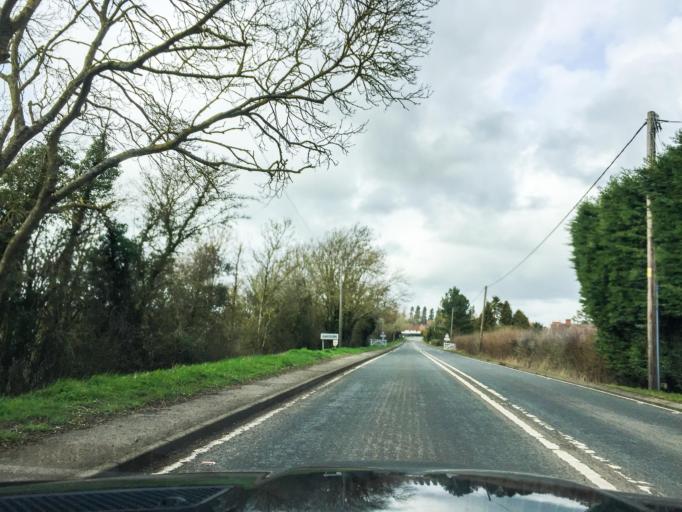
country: GB
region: England
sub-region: Warwickshire
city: Harbury
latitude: 52.1803
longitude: -1.4628
